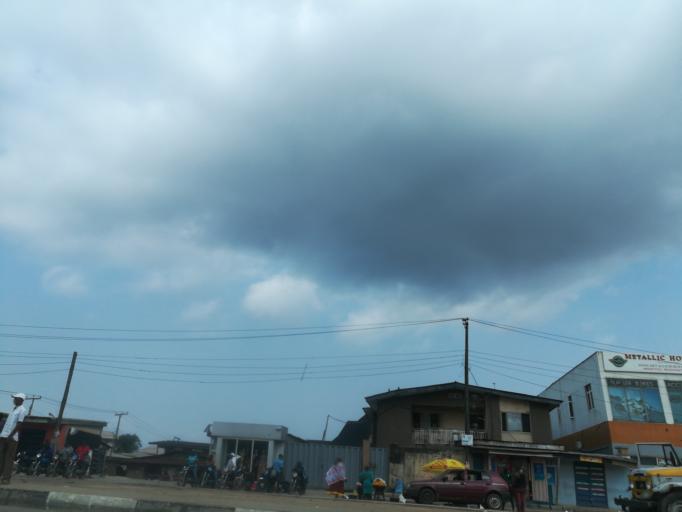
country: NG
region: Lagos
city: Ojota
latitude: 6.5719
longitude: 3.3975
